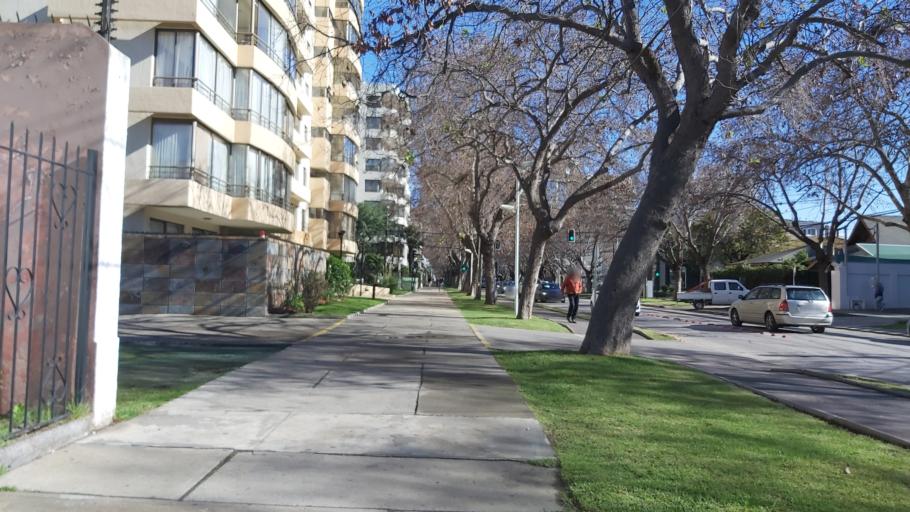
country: CL
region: Valparaiso
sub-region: Provincia de Valparaiso
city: Vina del Mar
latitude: -33.0161
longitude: -71.5455
